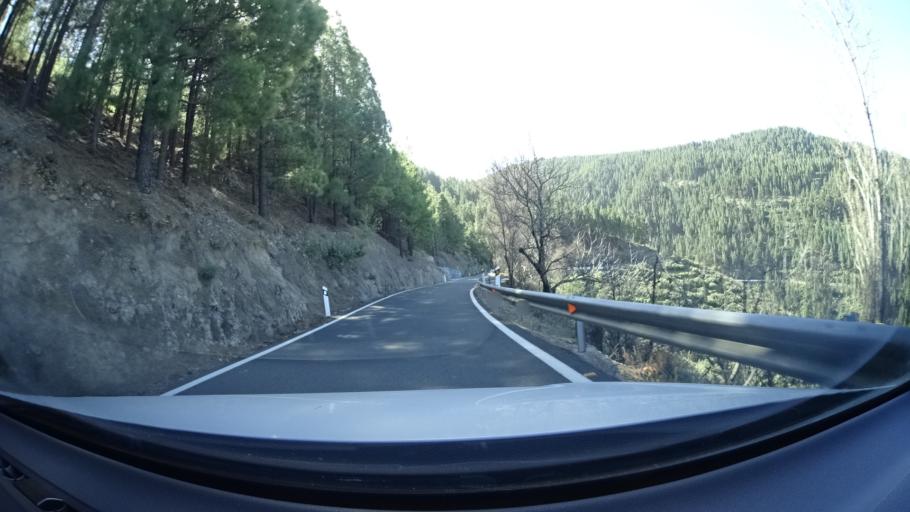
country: ES
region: Canary Islands
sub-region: Provincia de Las Palmas
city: Artenara
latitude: 28.0266
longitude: -15.6238
